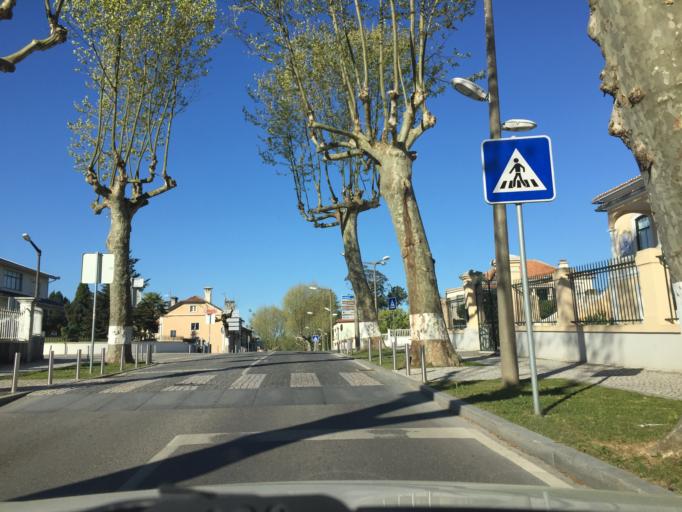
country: PT
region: Aveiro
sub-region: Anadia
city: Arcos
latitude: 40.4407
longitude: -8.4416
